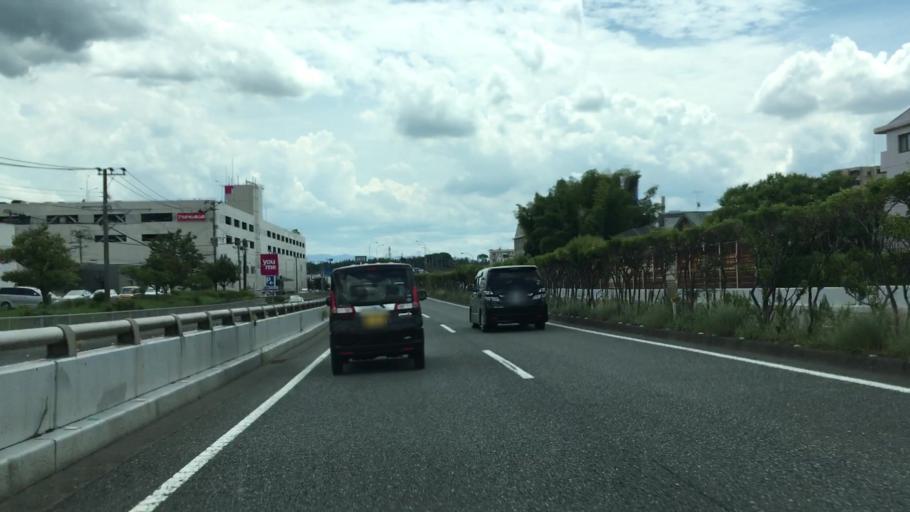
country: JP
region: Fukuoka
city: Chikushino-shi
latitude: 33.4860
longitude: 130.5366
